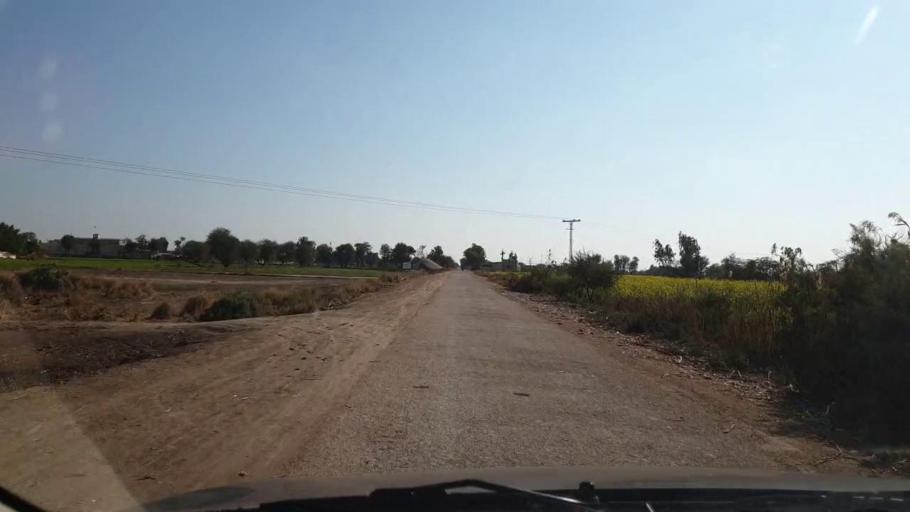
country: PK
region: Sindh
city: Sinjhoro
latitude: 25.9851
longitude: 68.8394
